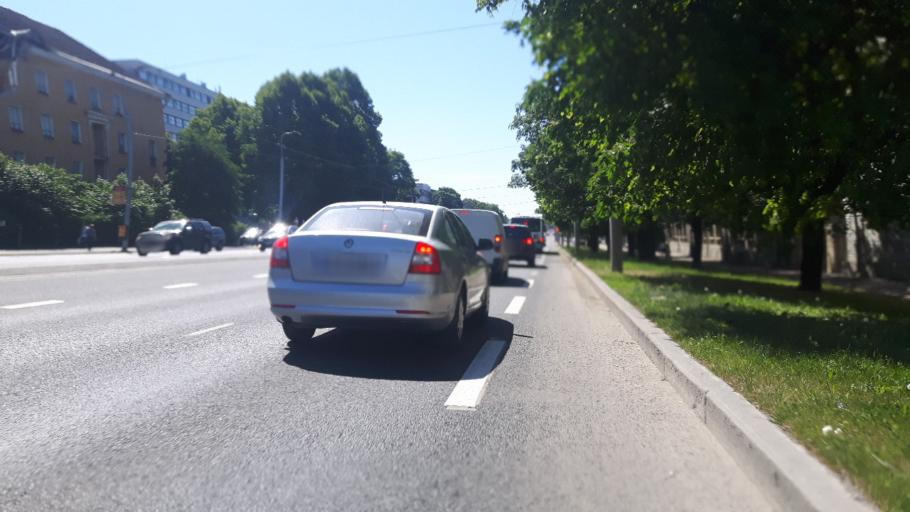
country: EE
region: Harju
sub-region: Tallinna linn
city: Tallinn
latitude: 59.4264
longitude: 24.7421
